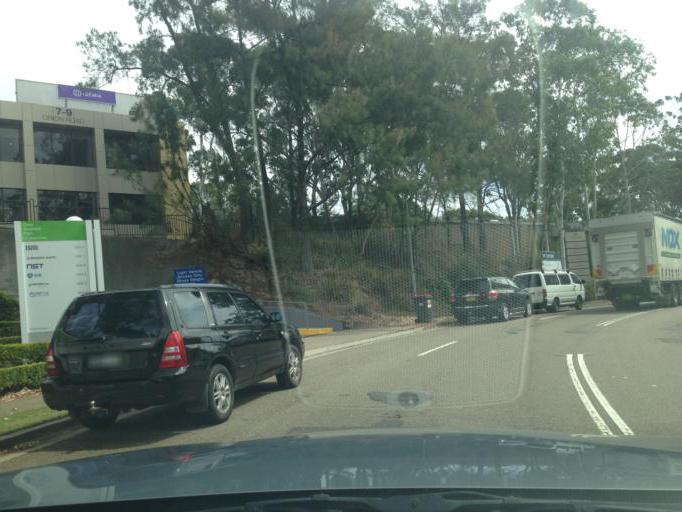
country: AU
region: New South Wales
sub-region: Lane Cove
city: Lane Cove West
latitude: -33.8080
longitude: 151.1489
